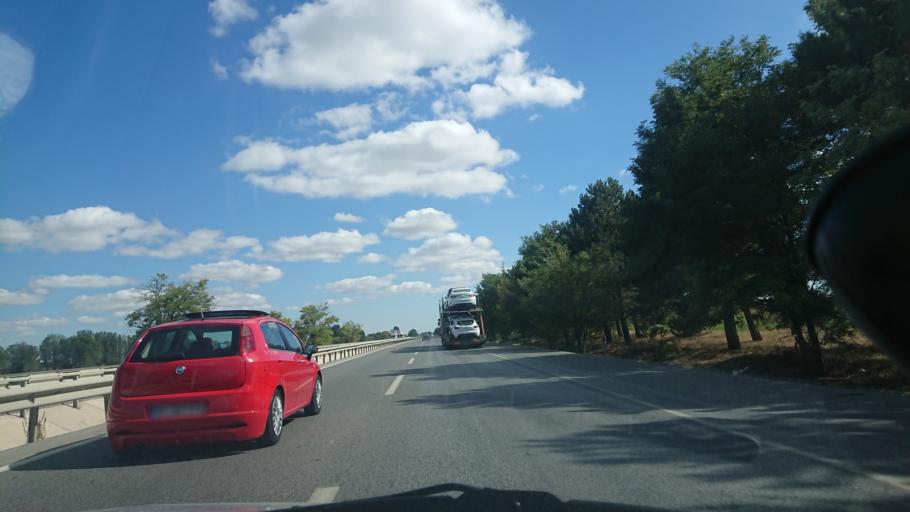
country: TR
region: Eskisehir
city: Sevinc
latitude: 39.6350
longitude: 30.8102
